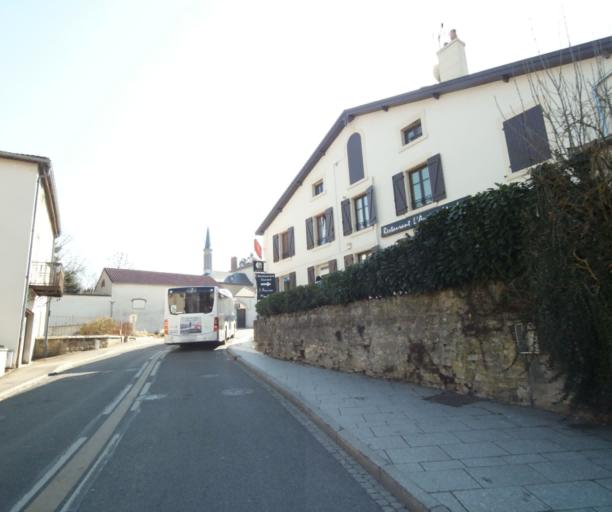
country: FR
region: Lorraine
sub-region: Departement de Meurthe-et-Moselle
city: Vandoeuvre-les-Nancy
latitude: 48.6466
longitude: 6.1756
